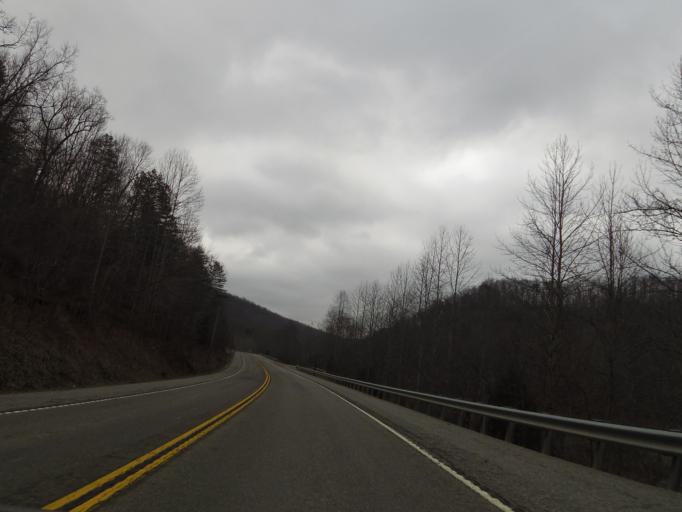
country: US
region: Tennessee
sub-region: Campbell County
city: Caryville
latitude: 36.4078
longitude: -84.2935
